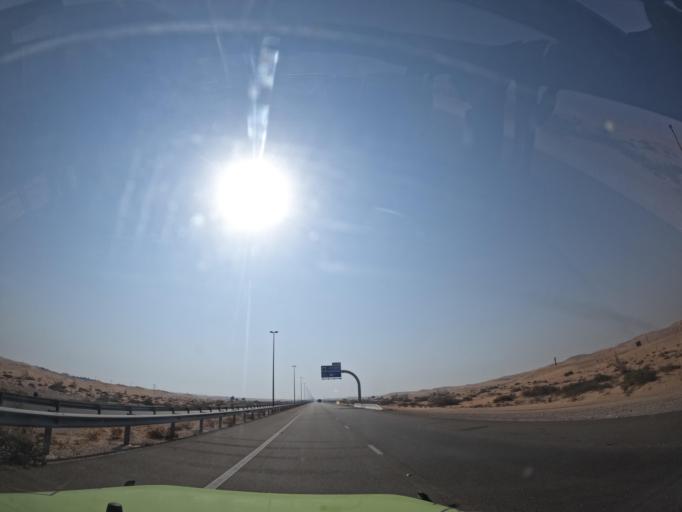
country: OM
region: Al Buraimi
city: Al Buraymi
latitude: 24.5166
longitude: 55.5586
